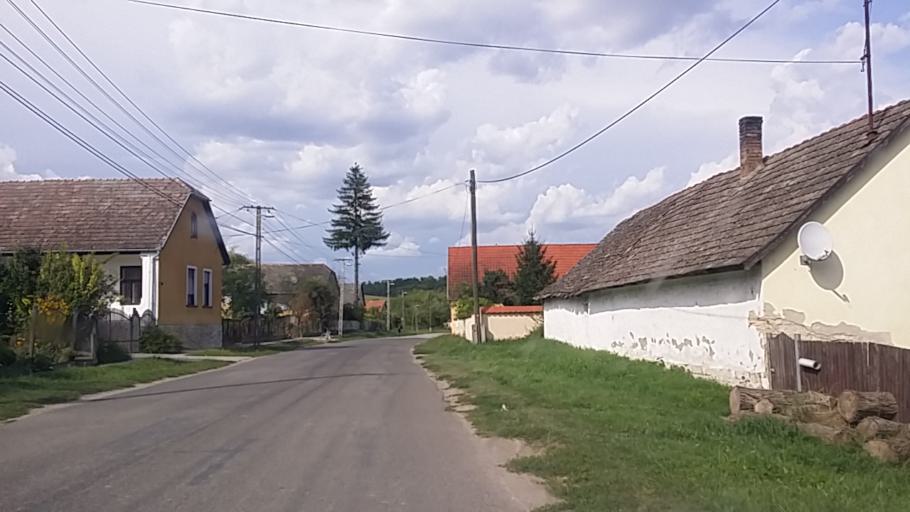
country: HU
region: Tolna
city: Zomba
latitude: 46.5020
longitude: 18.5678
